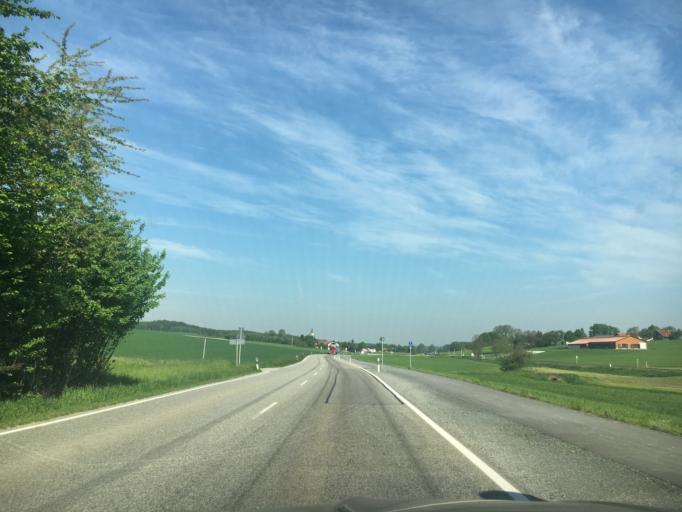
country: DE
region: Bavaria
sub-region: Upper Bavaria
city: Neumarkt-Sankt Veit
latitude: 48.3686
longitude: 12.4916
